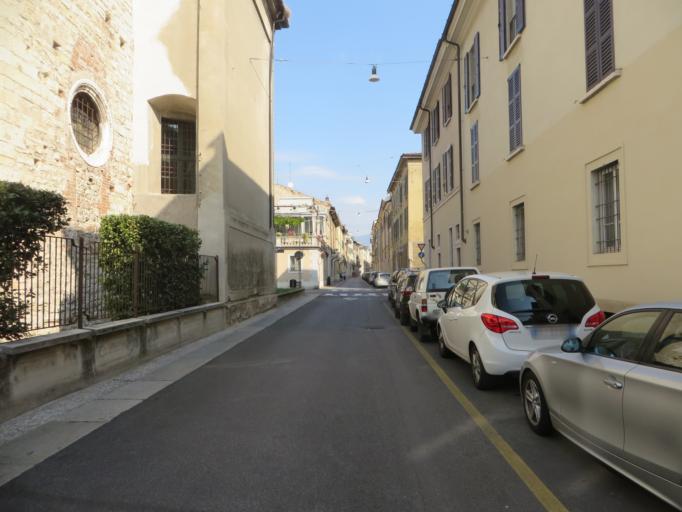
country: IT
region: Lombardy
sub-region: Provincia di Brescia
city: Brescia
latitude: 45.5391
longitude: 10.2123
